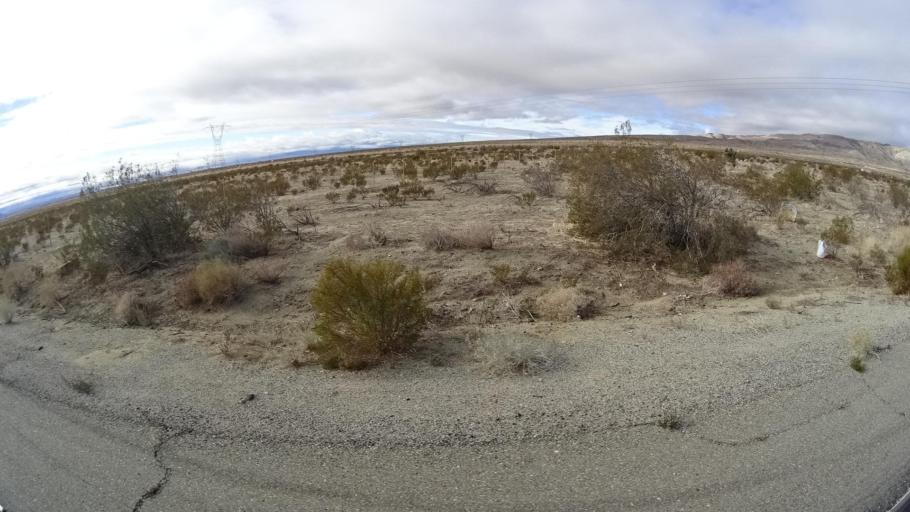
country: US
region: California
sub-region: Kern County
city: Mojave
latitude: 34.9803
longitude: -118.3137
